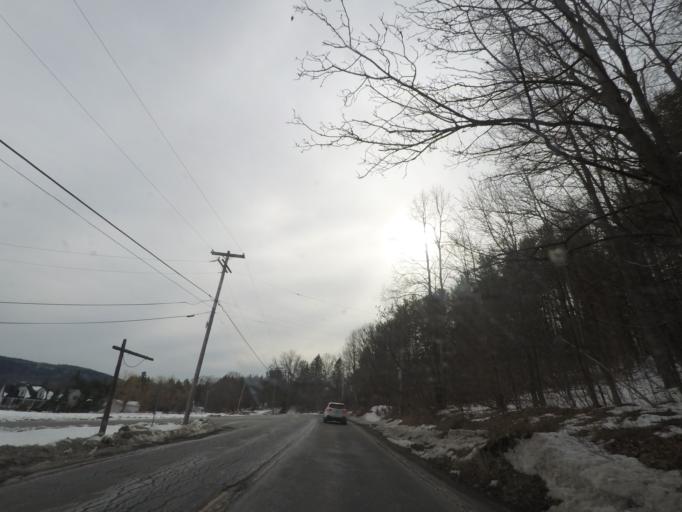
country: US
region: New York
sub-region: Albany County
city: Altamont
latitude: 42.6430
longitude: -74.1385
